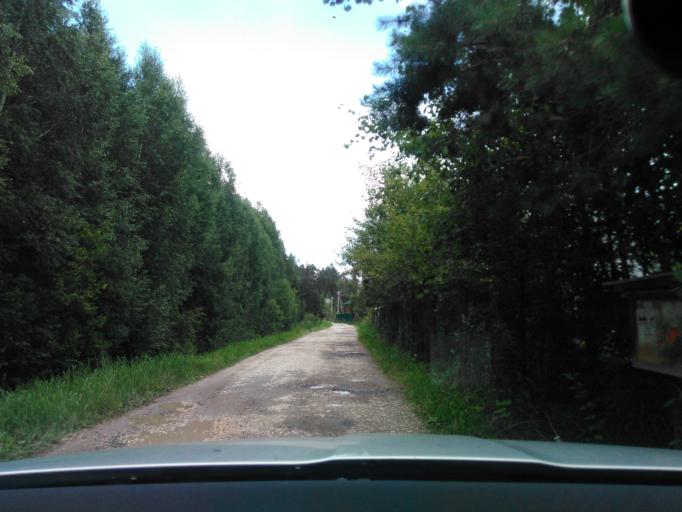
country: RU
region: Moskovskaya
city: Mendeleyevo
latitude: 56.0870
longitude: 37.2572
